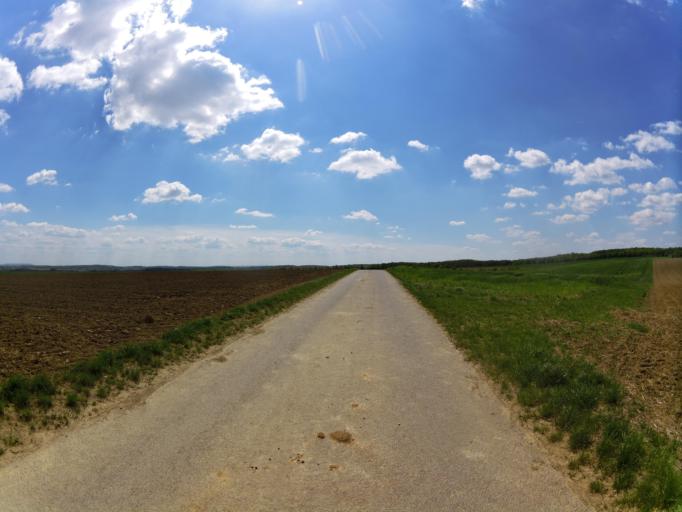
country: DE
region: Bavaria
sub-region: Regierungsbezirk Unterfranken
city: Unterpleichfeld
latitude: 49.8802
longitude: 10.0034
